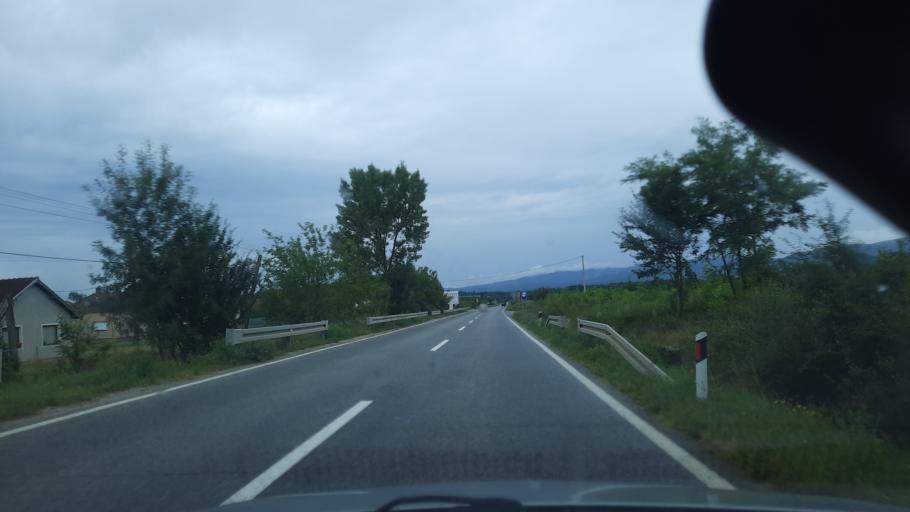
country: RS
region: Central Serbia
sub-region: Sumadijski Okrug
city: Knic
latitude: 43.9243
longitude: 20.7734
